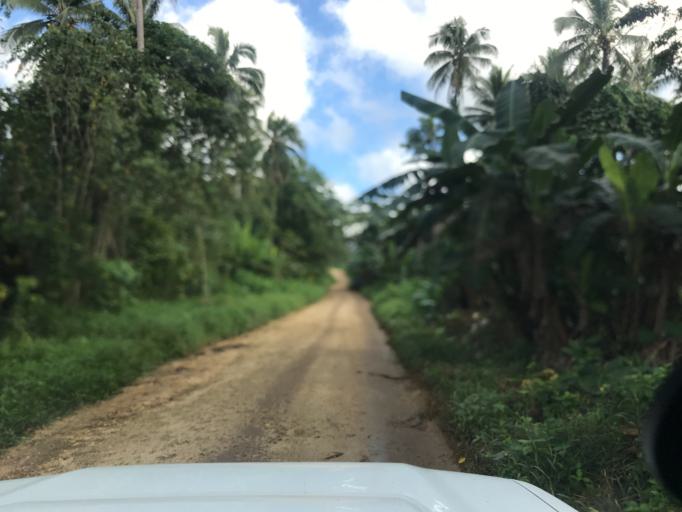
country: VU
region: Sanma
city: Luganville
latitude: -15.5102
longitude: 167.1147
